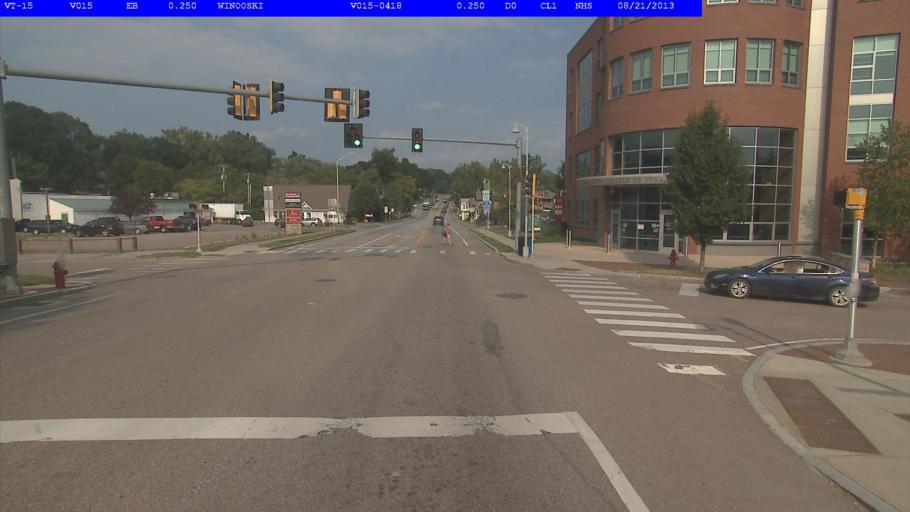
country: US
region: Vermont
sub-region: Chittenden County
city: Winooski
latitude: 44.4915
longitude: -73.1822
